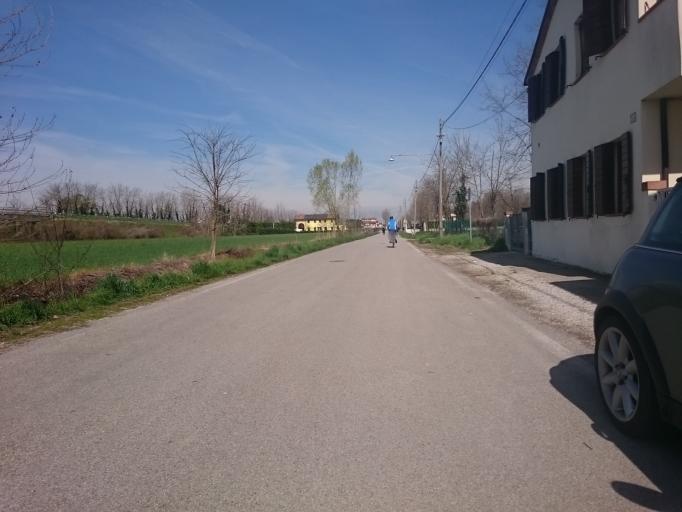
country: IT
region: Veneto
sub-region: Provincia di Padova
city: Villaguattera
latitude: 45.4354
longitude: 11.8380
